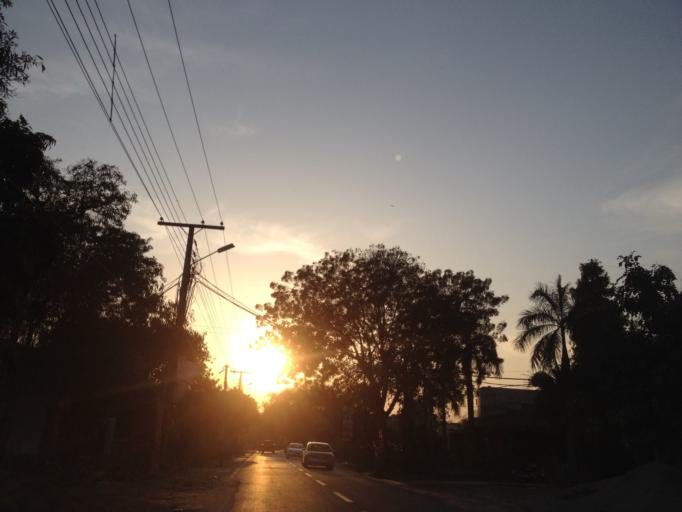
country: PK
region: Punjab
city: Lahore
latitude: 31.4919
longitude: 74.3168
